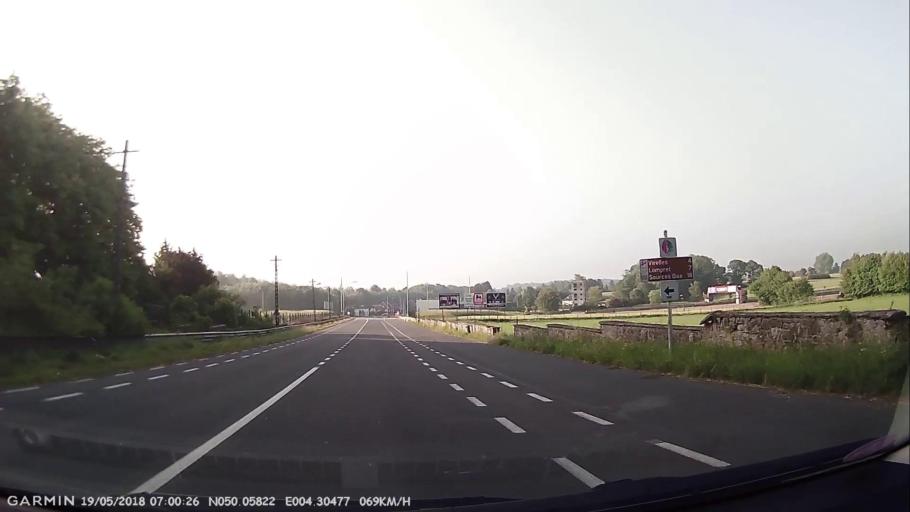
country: BE
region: Wallonia
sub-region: Province du Hainaut
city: Chimay
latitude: 50.0580
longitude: 4.3050
